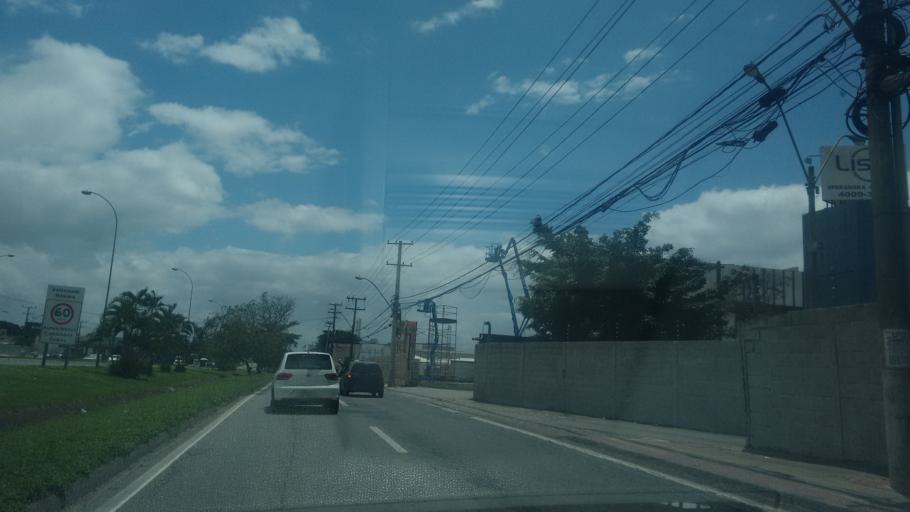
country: BR
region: Espirito Santo
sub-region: Serra
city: Serra
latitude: -20.2036
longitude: -40.2690
